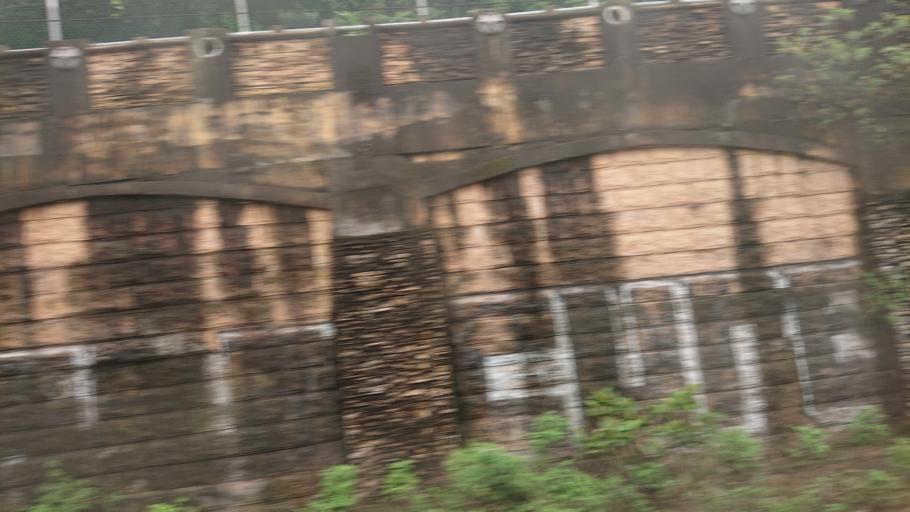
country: TW
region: Taiwan
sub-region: Keelung
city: Keelung
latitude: 25.0826
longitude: 121.7040
